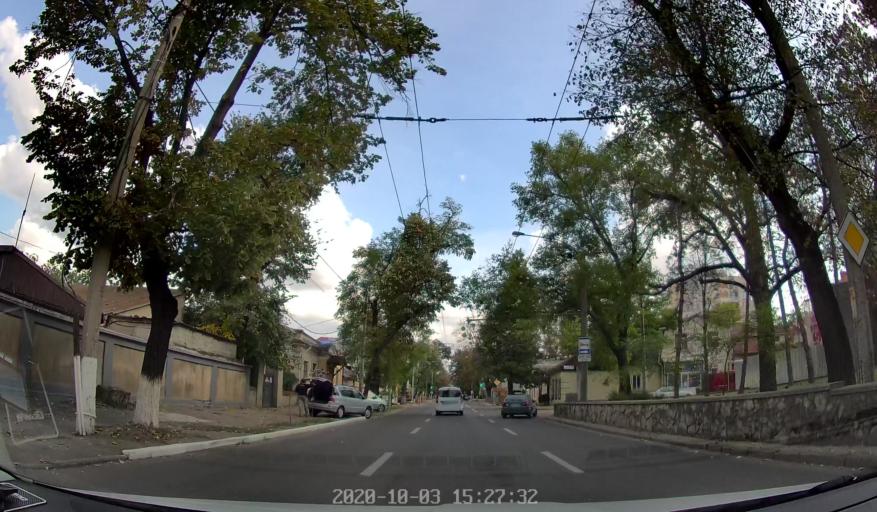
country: MD
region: Chisinau
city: Chisinau
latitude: 47.0241
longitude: 28.8183
